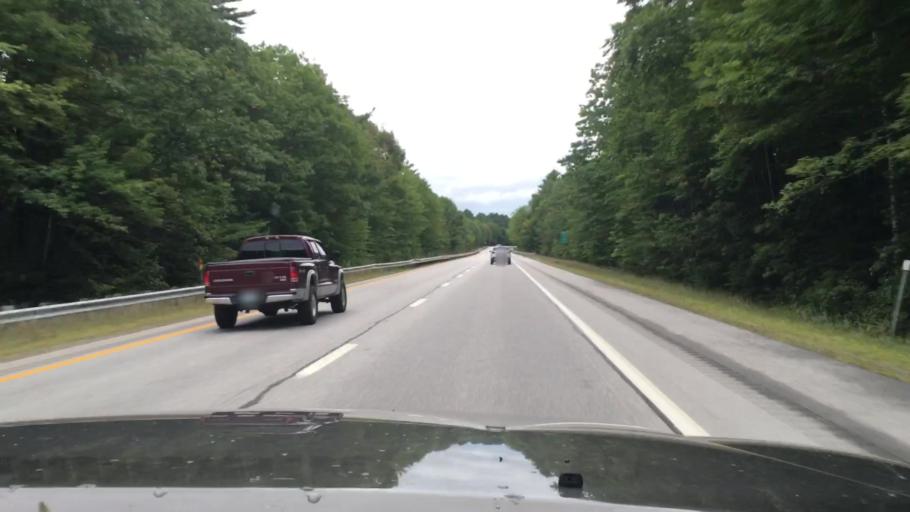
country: US
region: New Hampshire
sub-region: Belknap County
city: Sanbornton
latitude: 43.5402
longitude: -71.6157
